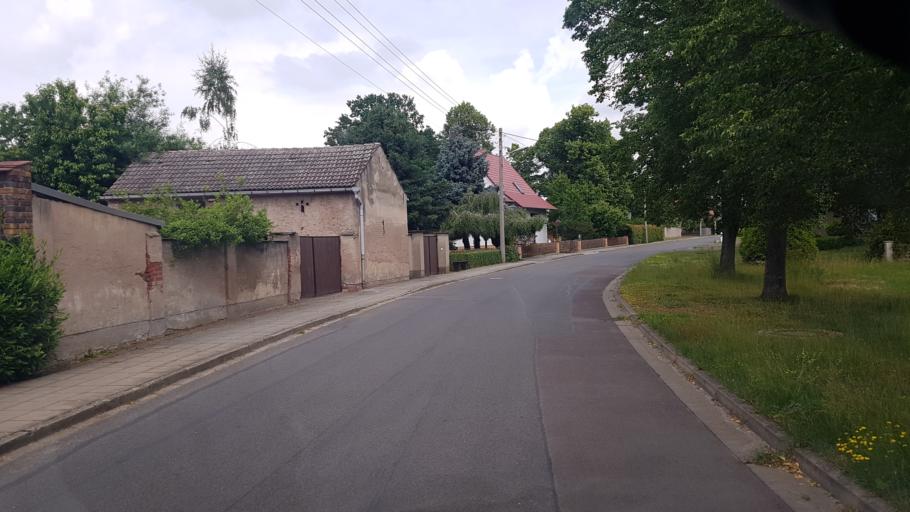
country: DE
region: Brandenburg
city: Lebusa
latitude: 51.8166
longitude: 13.4503
